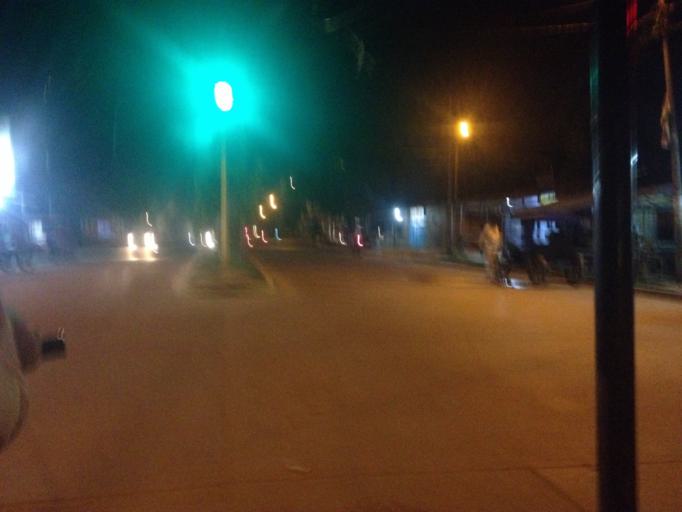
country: PE
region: Ucayali
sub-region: Provincia de Coronel Portillo
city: Pucallpa
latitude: -8.3995
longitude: -74.5668
